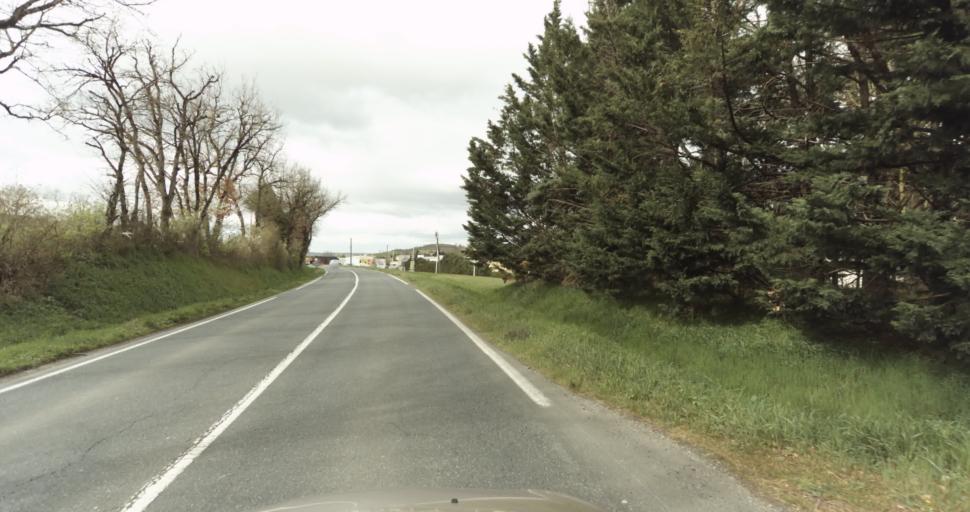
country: FR
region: Midi-Pyrenees
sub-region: Departement du Tarn
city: Puygouzon
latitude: 43.8879
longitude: 2.1660
